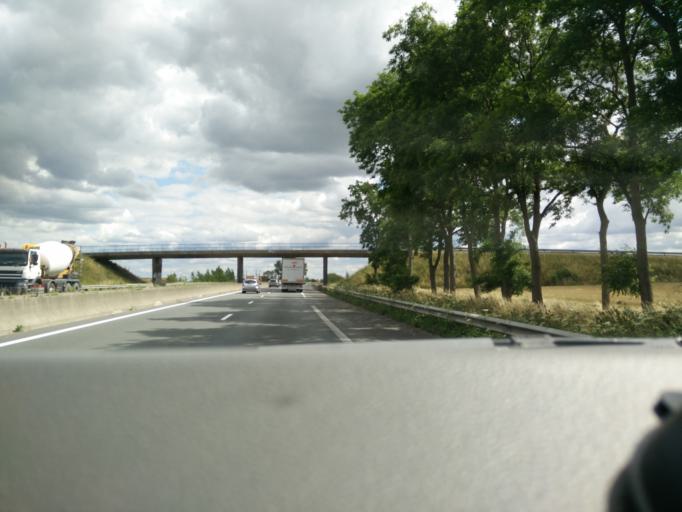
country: FR
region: Nord-Pas-de-Calais
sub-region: Departement du Nord
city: Quaedypre
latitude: 50.9374
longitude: 2.4631
